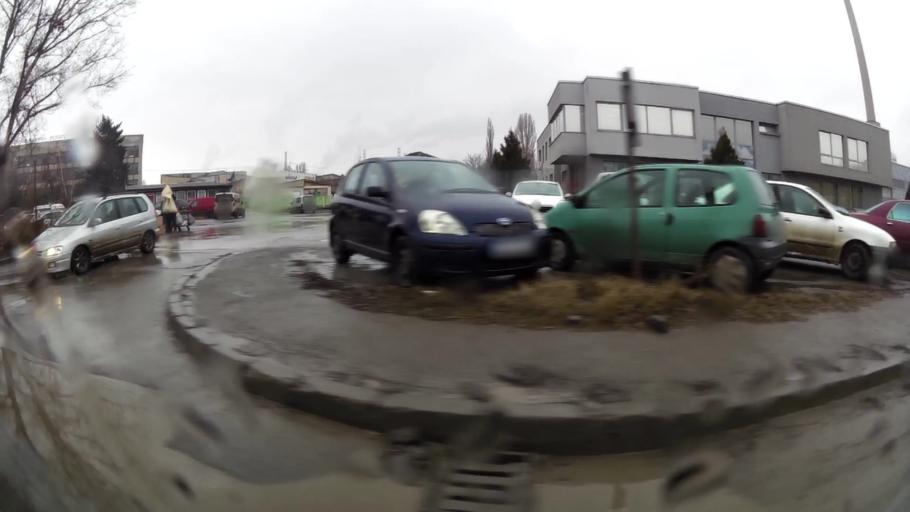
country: BG
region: Sofia-Capital
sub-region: Stolichna Obshtina
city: Sofia
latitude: 42.6622
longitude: 23.4184
